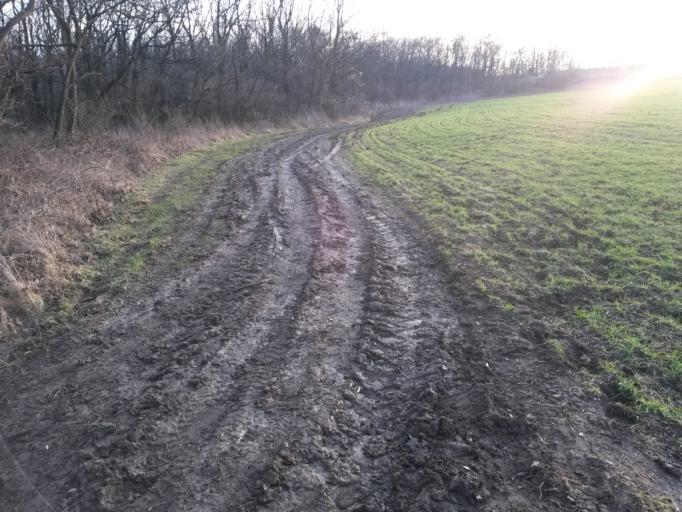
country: HU
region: Pest
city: Perbal
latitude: 47.5943
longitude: 18.7348
